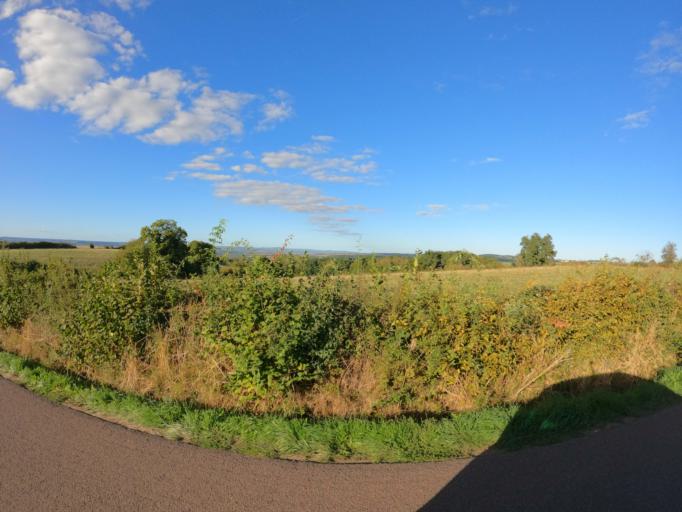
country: FR
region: Bourgogne
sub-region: Departement de Saone-et-Loire
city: Ecuisses
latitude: 46.7394
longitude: 4.5487
